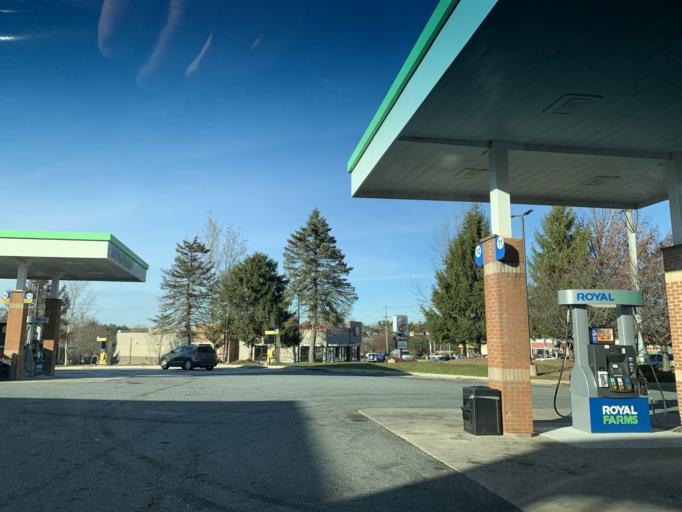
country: US
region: Maryland
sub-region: Cecil County
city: Elkton
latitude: 39.5991
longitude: -75.8279
